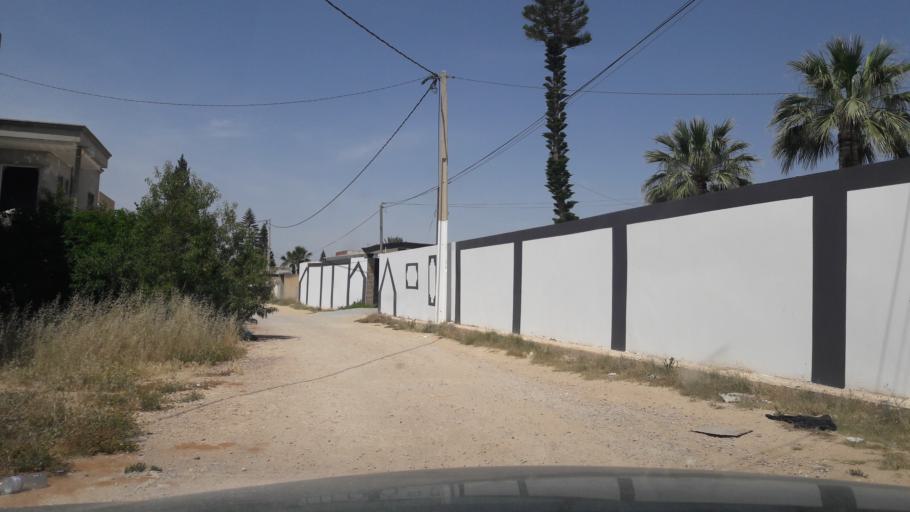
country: TN
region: Safaqis
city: Al Qarmadah
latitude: 34.7883
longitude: 10.7598
